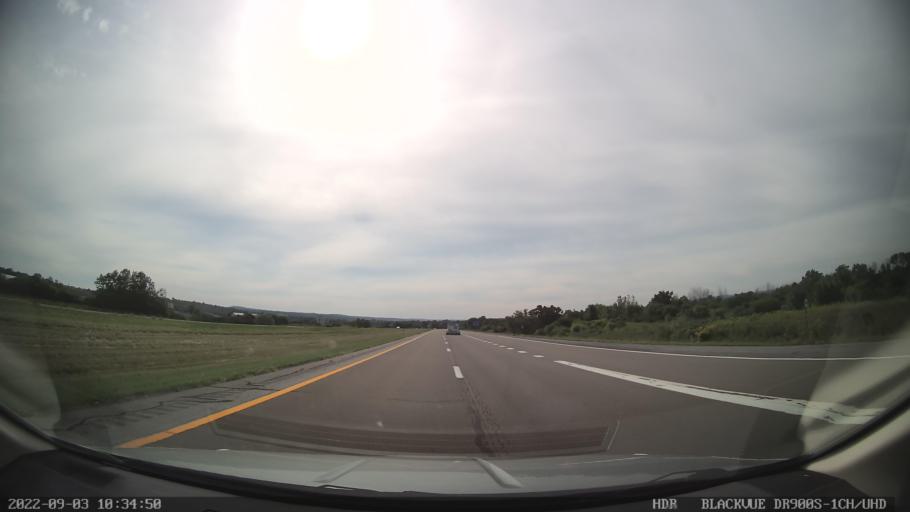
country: US
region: New York
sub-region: Livingston County
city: Mount Morris
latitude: 42.7329
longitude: -77.8357
